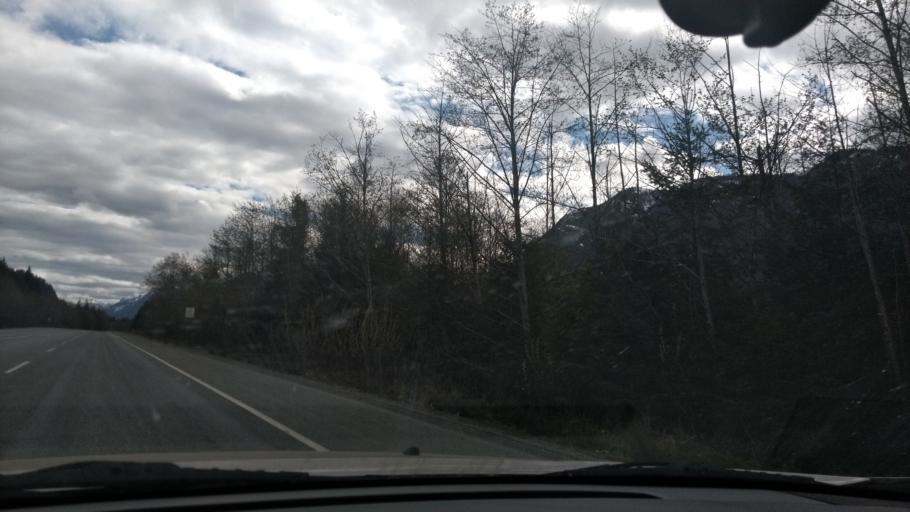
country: CA
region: British Columbia
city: Campbell River
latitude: 49.8694
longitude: -125.6280
